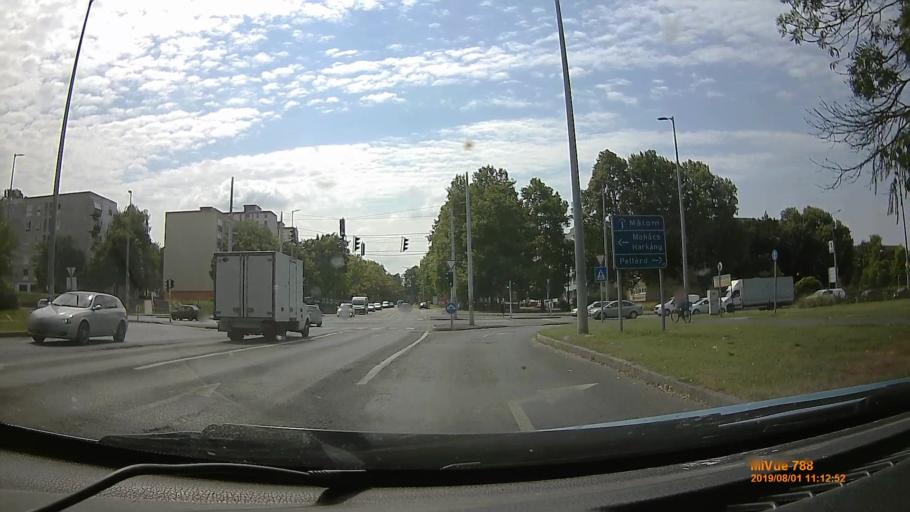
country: HU
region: Baranya
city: Pecs
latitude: 46.0428
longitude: 18.2157
